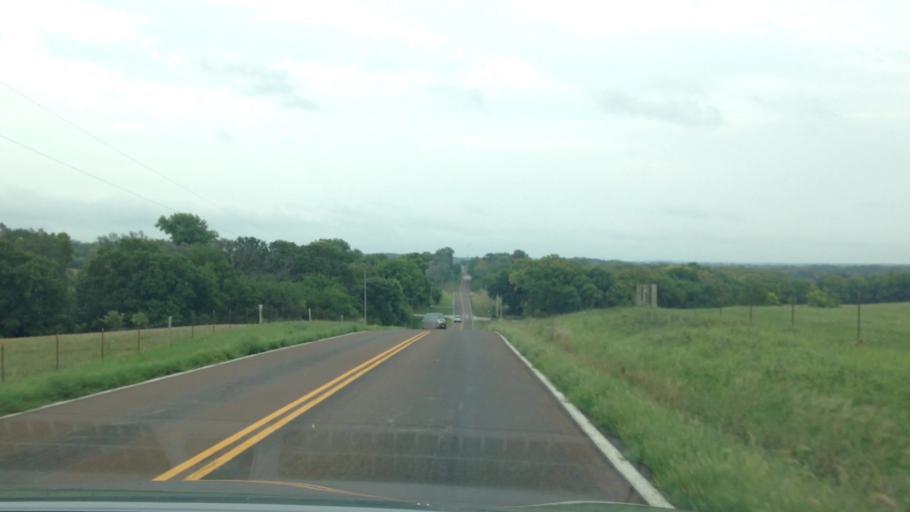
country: US
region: Missouri
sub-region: Clay County
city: Smithville
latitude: 39.4050
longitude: -94.6330
